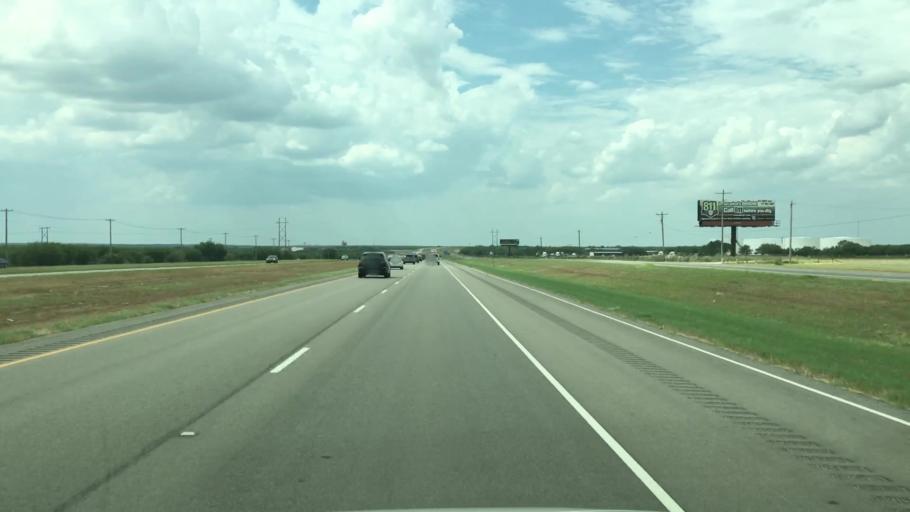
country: US
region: Texas
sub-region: Live Oak County
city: Three Rivers
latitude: 28.5094
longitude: -98.1668
